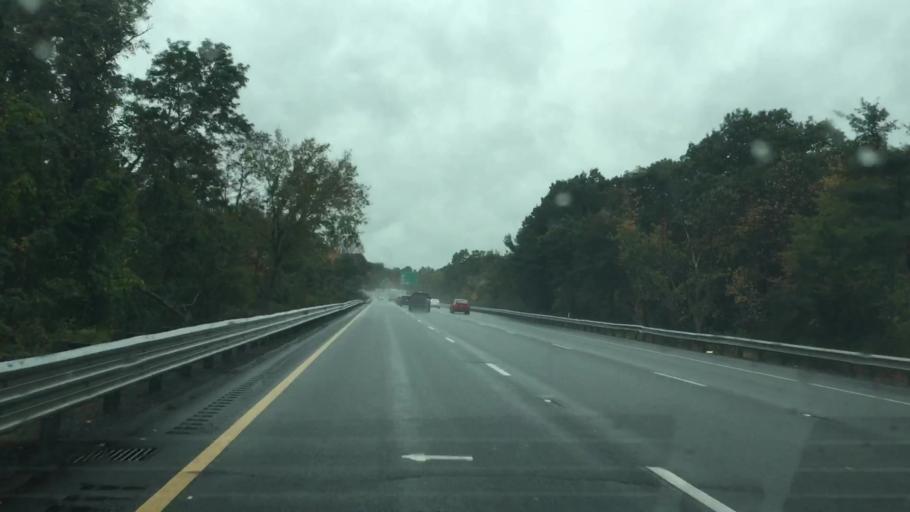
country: US
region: Massachusetts
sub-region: Essex County
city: Haverhill
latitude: 42.8049
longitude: -71.0636
